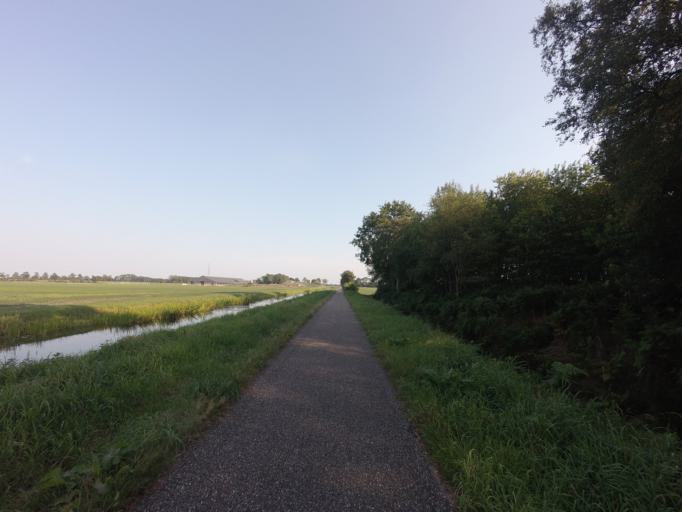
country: NL
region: Drenthe
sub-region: Gemeente Tynaarlo
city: Vries
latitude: 53.1200
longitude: 6.5017
